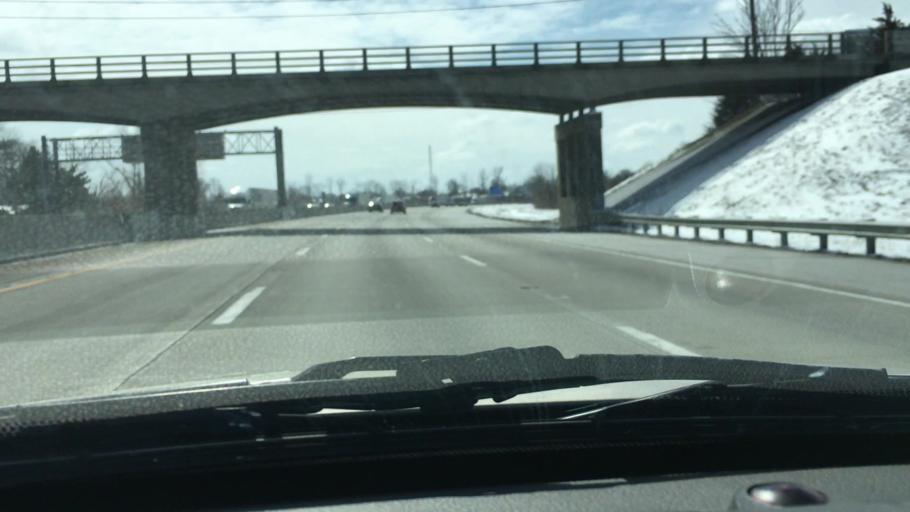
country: US
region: Indiana
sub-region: Marion County
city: Warren Park
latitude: 39.7620
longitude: -86.0287
